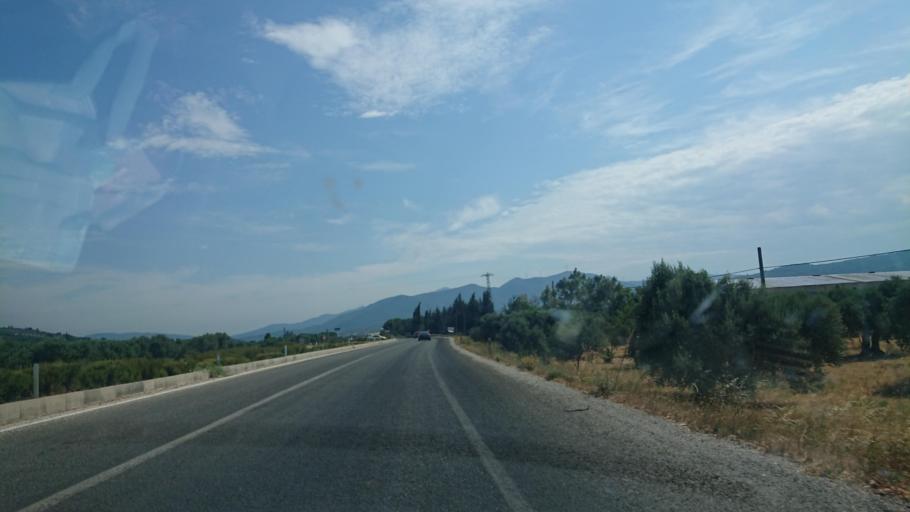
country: TR
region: Izmir
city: Dagkizilca
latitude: 38.2491
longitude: 27.3809
